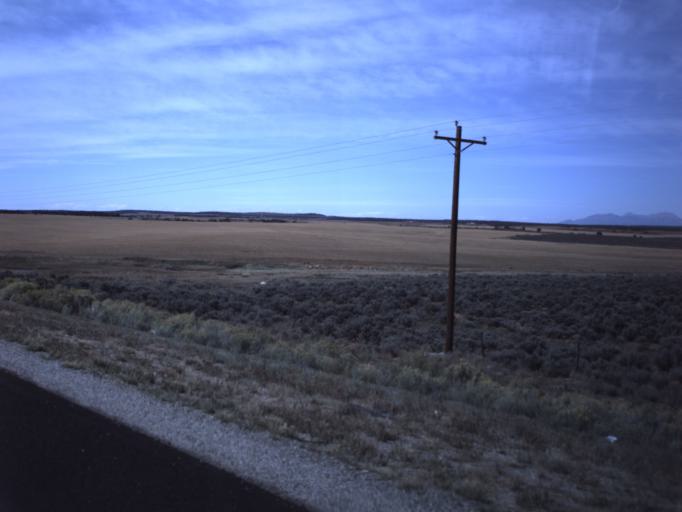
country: US
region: Colorado
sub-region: Dolores County
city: Dove Creek
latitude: 37.8175
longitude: -109.0455
